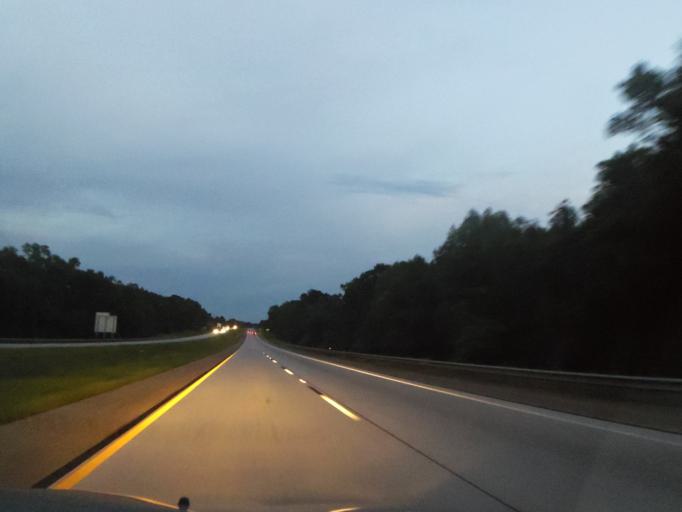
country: US
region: Georgia
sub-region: McDuffie County
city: Thomson
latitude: 33.5128
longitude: -82.4892
